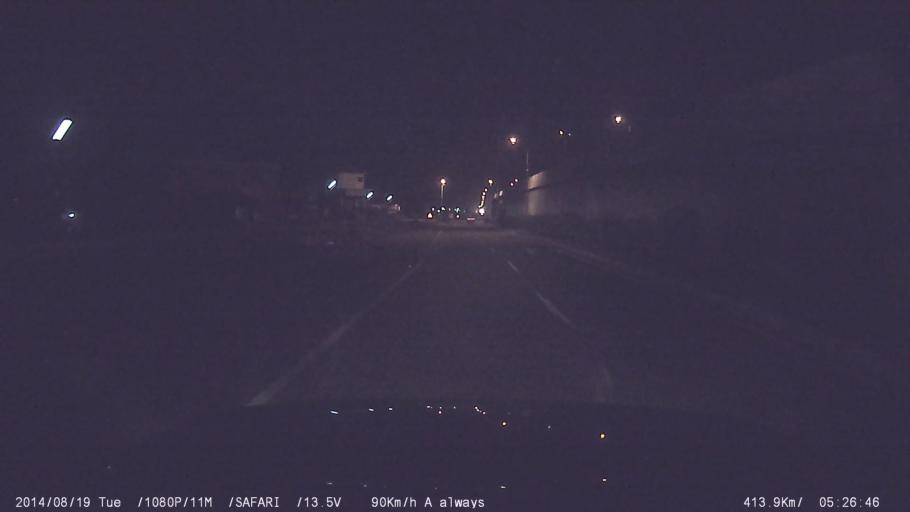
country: IN
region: Tamil Nadu
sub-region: Salem
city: Attayyampatti
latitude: 11.5843
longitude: 78.0583
